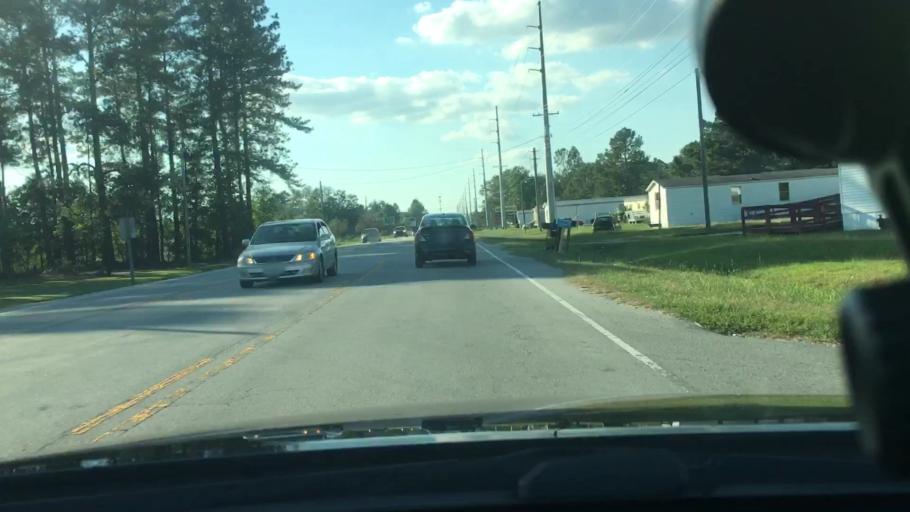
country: US
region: North Carolina
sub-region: Pitt County
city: Windsor
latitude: 35.5580
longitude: -77.3360
